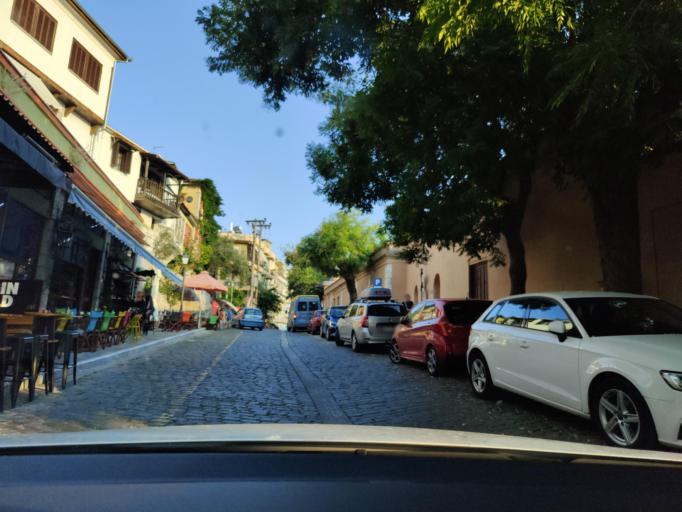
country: GR
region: East Macedonia and Thrace
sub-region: Nomos Kavalas
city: Kavala
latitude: 40.9338
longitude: 24.4137
